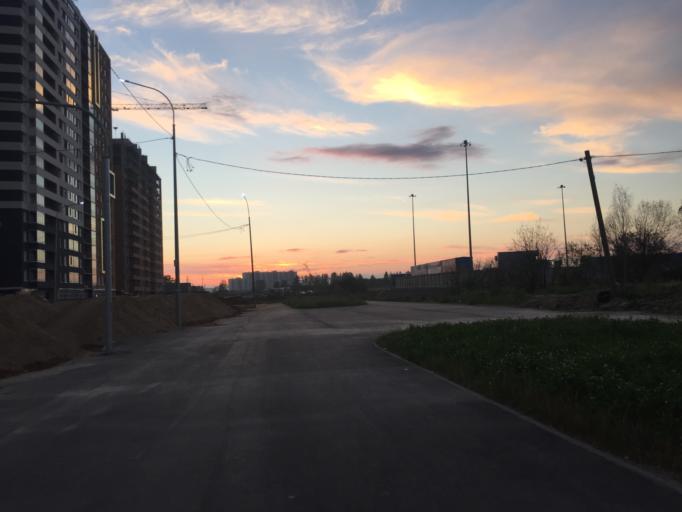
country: RU
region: Leningrad
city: Murino
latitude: 60.0687
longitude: 30.4294
